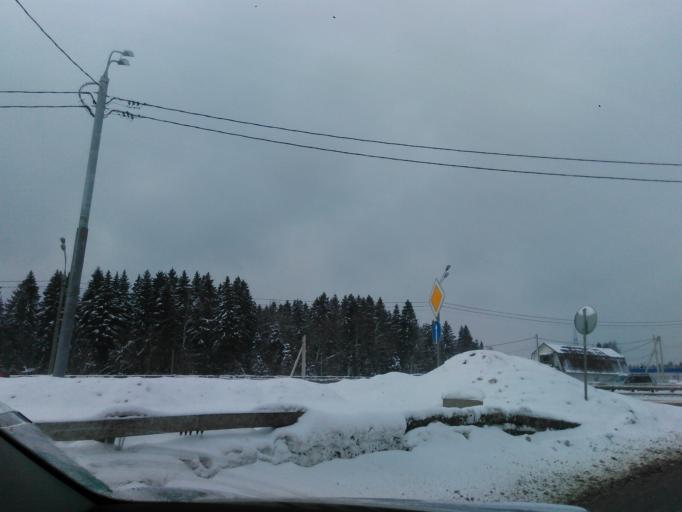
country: RU
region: Moskovskaya
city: Yermolino
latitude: 56.1379
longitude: 37.4967
